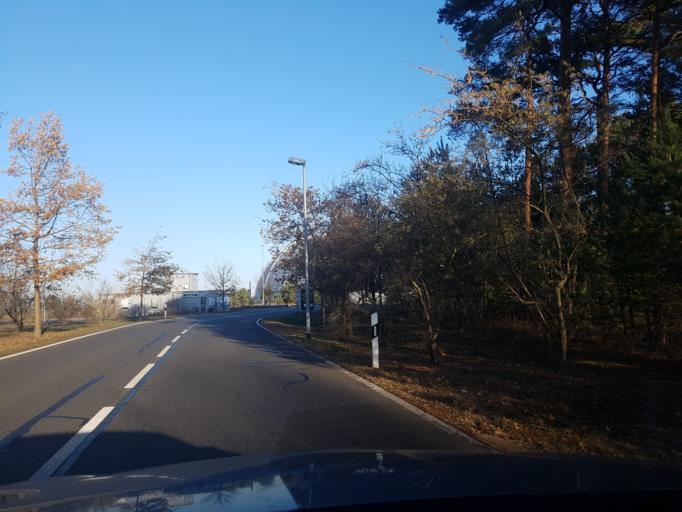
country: DE
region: Brandenburg
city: Halbe
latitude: 52.0317
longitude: 13.7481
